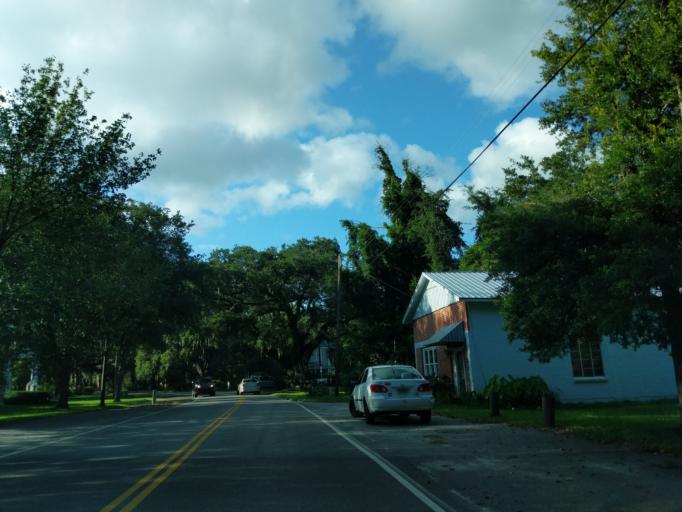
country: US
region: South Carolina
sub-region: Charleston County
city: Awendaw
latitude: 33.0871
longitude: -79.4608
